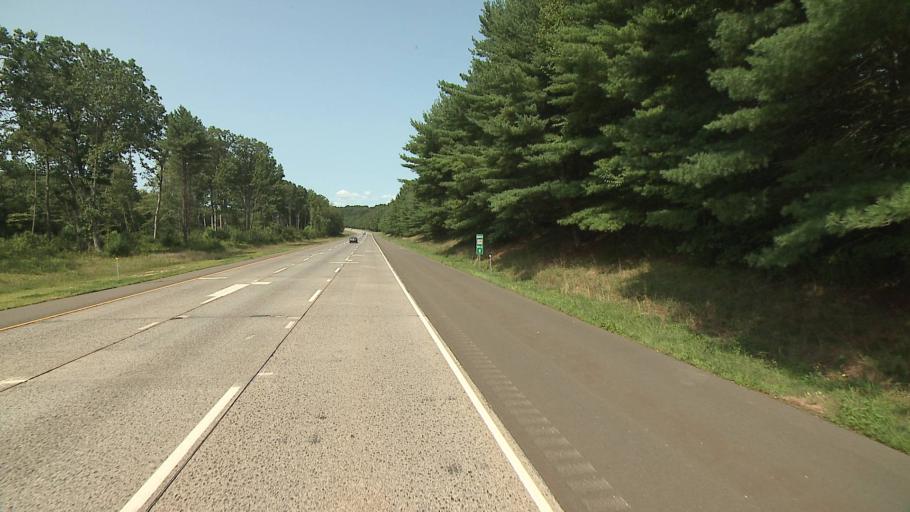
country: US
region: Connecticut
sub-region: Fairfield County
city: Trumbull
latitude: 41.2706
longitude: -73.2107
